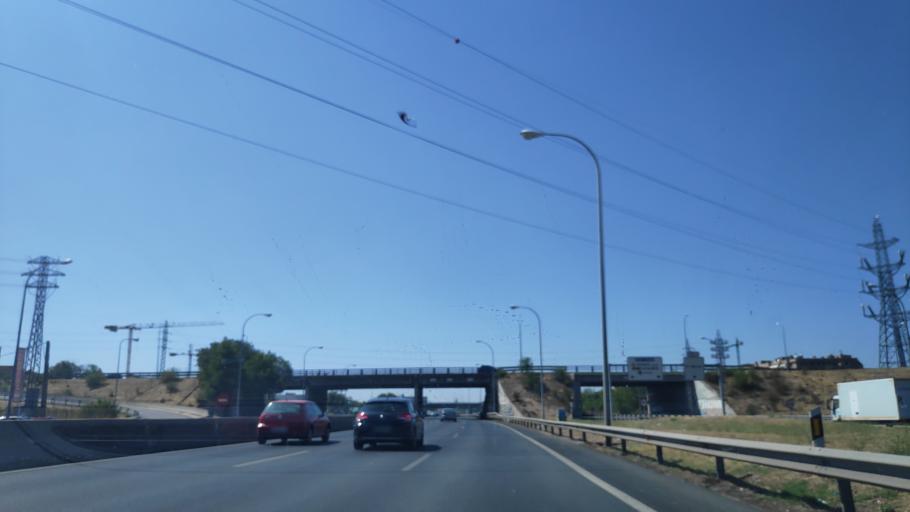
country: ES
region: Madrid
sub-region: Provincia de Madrid
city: Getafe
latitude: 40.3235
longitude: -3.7299
